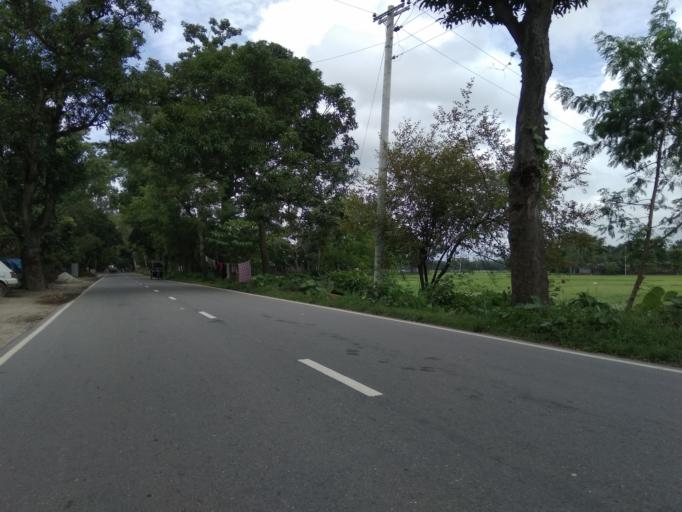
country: BD
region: Rajshahi
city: Saidpur
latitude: 25.7722
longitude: 88.7990
